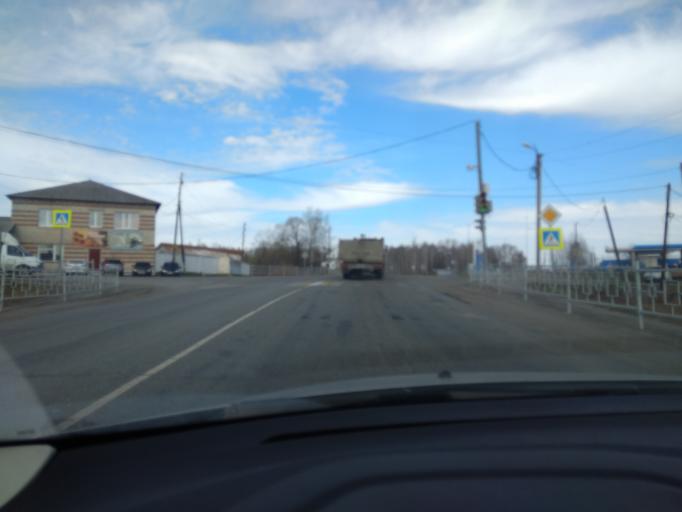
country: RU
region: Sverdlovsk
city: Pyshma
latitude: 56.9512
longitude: 63.2267
